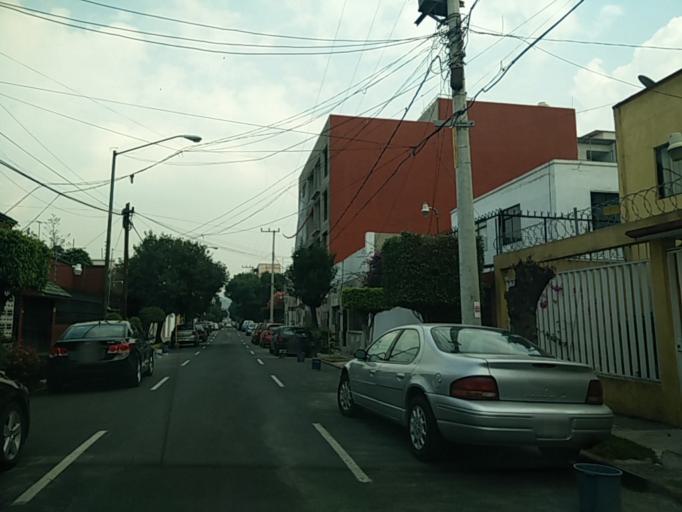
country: MX
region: Mexico
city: Colonia Lindavista
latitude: 19.4857
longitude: -99.1280
